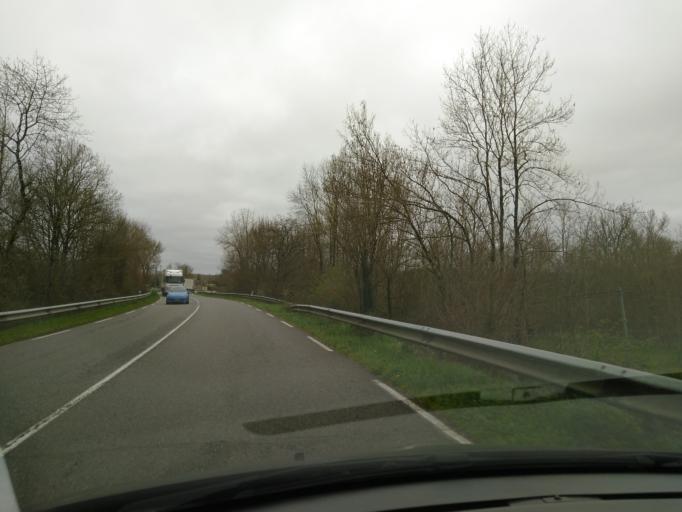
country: FR
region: Aquitaine
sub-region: Departement du Lot-et-Garonne
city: Castillonnes
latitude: 44.6722
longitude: 0.5801
